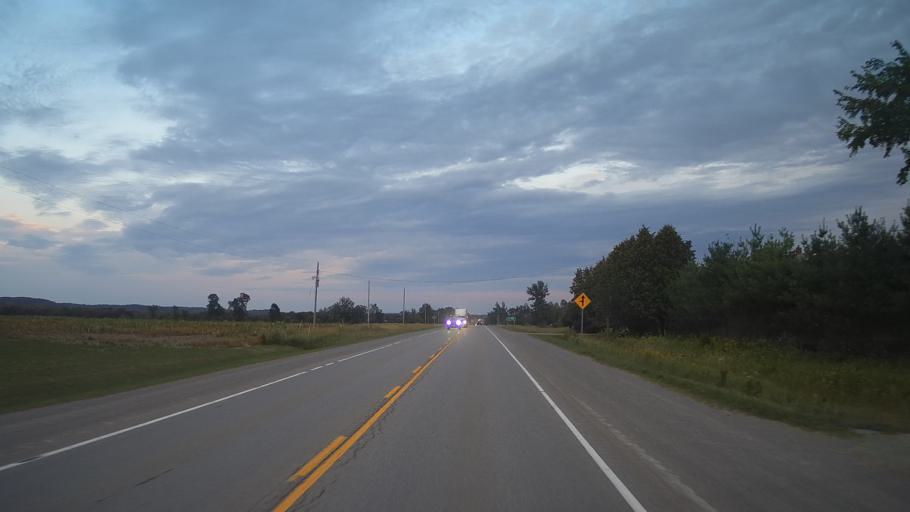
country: CA
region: Ontario
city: Pembroke
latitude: 45.7012
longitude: -76.9664
